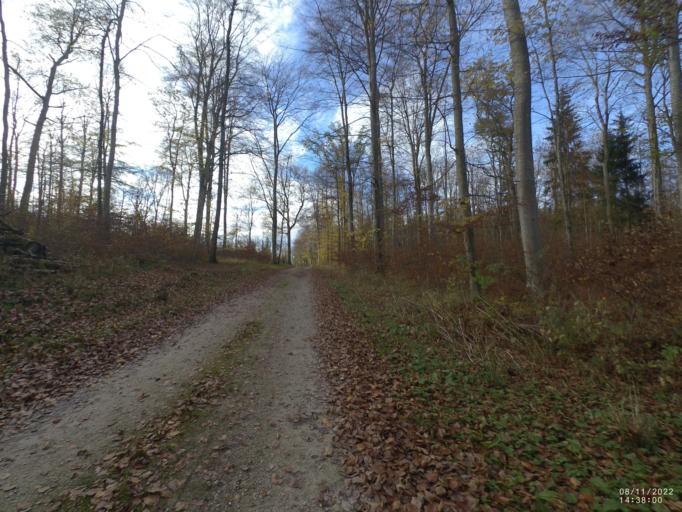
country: DE
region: Baden-Wuerttemberg
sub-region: Regierungsbezirk Stuttgart
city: Bad Uberkingen
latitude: 48.5717
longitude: 9.8286
